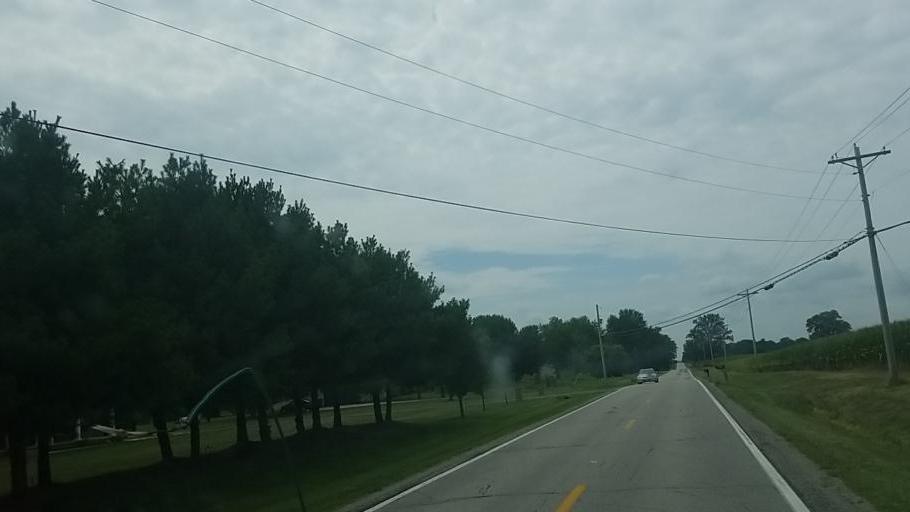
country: US
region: Ohio
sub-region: Franklin County
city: Groveport
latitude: 39.8271
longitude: -82.8744
